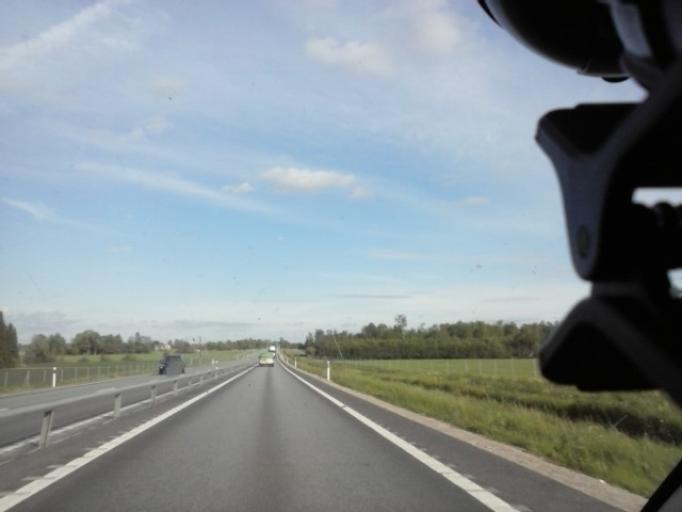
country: EE
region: Jogevamaa
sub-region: Tabivere vald
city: Tabivere
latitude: 58.4370
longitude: 26.4648
